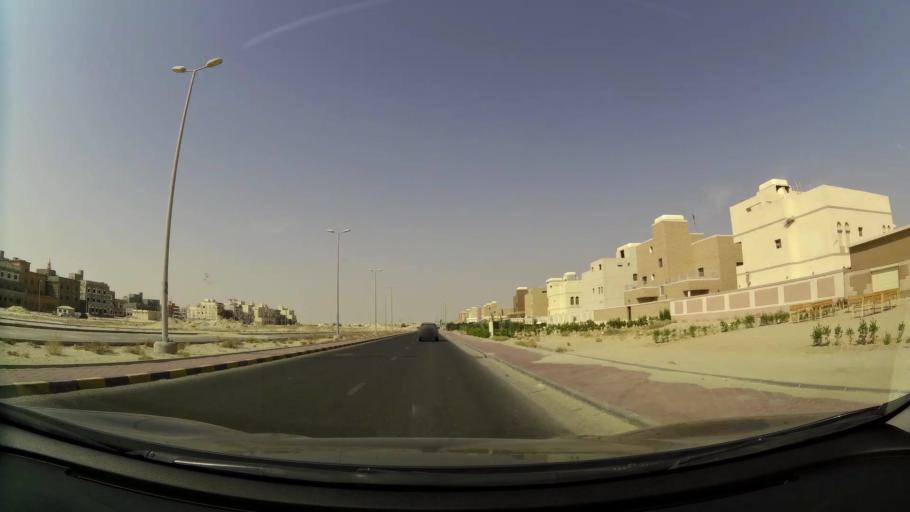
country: KW
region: Al Ahmadi
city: Al Wafrah
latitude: 28.8020
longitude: 48.0502
